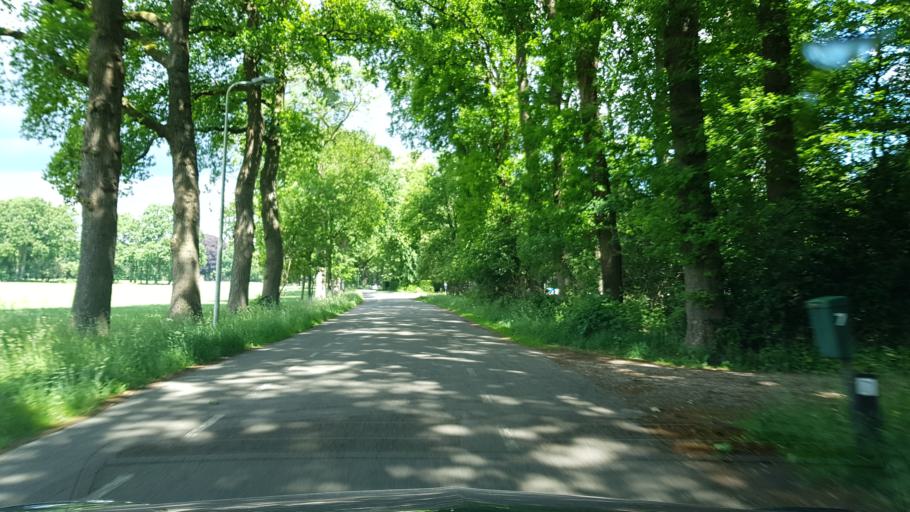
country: NL
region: Gelderland
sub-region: Gemeente Epe
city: Epe
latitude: 52.3529
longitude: 5.9210
